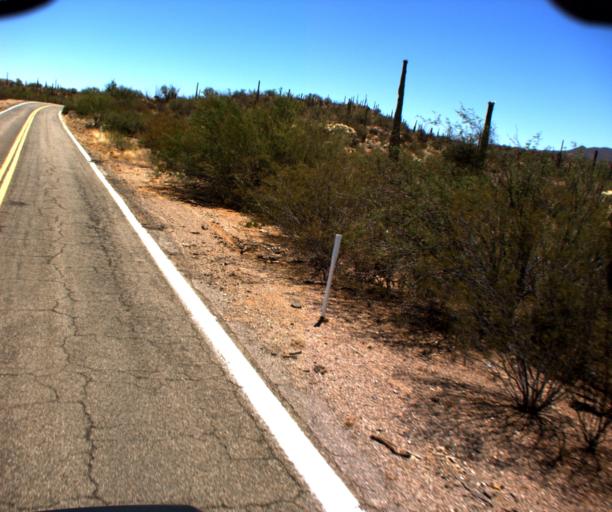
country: US
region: Arizona
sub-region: Pima County
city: Sells
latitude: 32.1732
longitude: -112.2152
